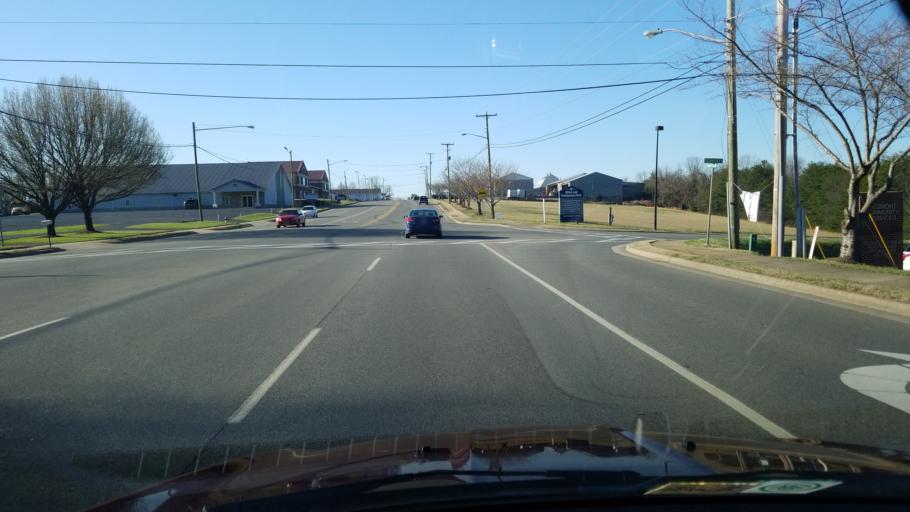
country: US
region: Virginia
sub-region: Franklin County
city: Rocky Mount
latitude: 37.0152
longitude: -79.8924
